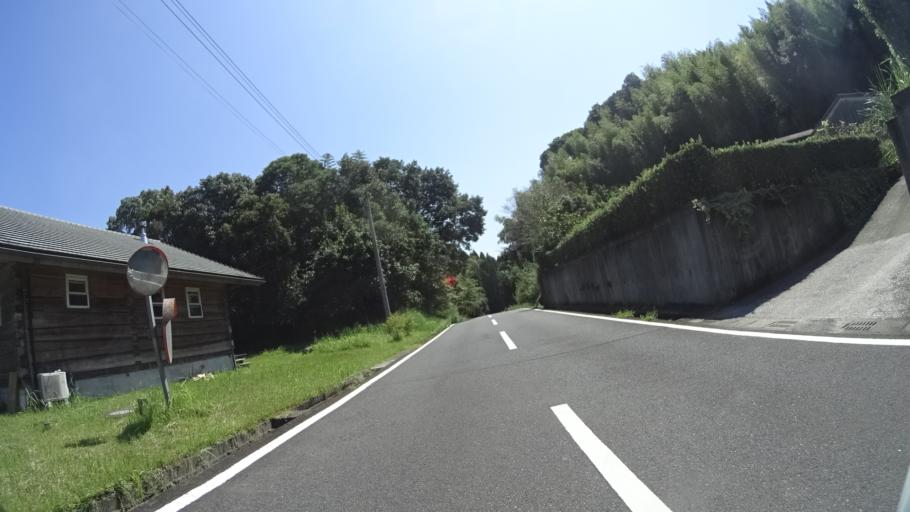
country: JP
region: Kagoshima
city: Kajiki
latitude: 31.7602
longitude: 130.6711
